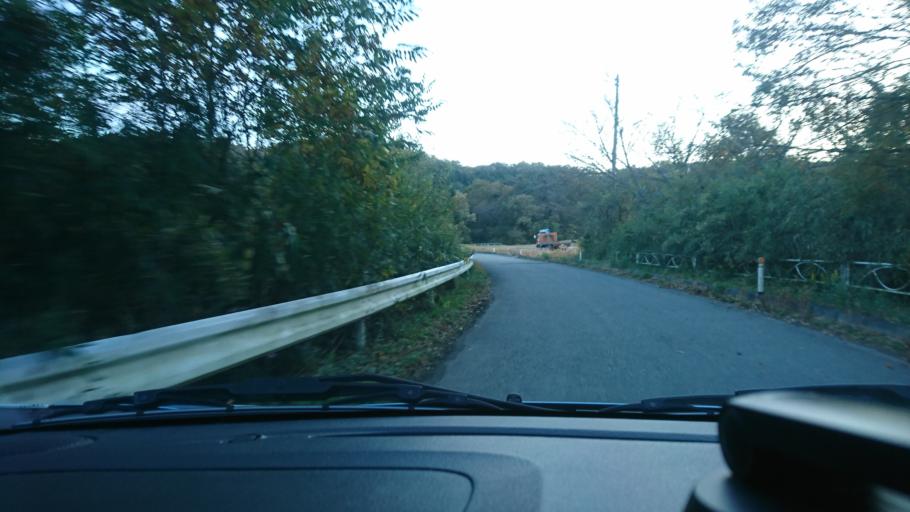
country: JP
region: Iwate
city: Ichinoseki
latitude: 38.7707
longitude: 141.2303
